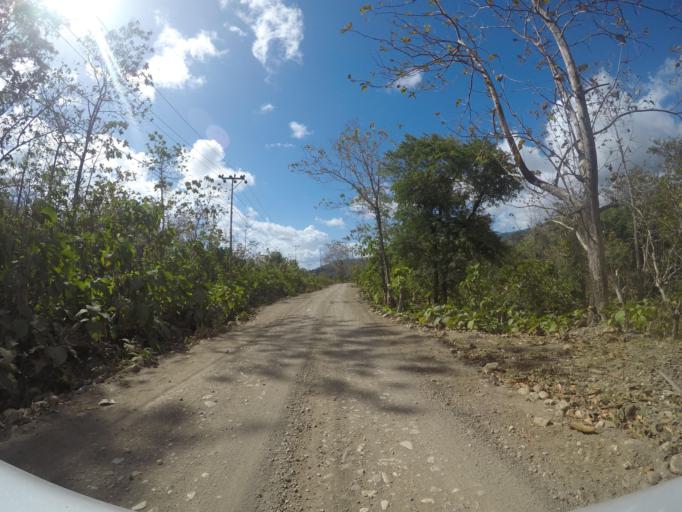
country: TL
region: Lautem
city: Lospalos
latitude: -8.5236
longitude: 126.8416
